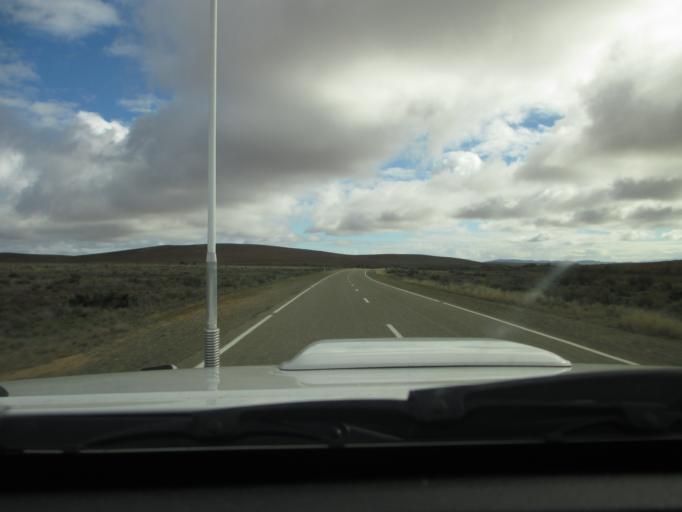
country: AU
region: South Australia
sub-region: Flinders Ranges
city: Quorn
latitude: -32.1405
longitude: 138.5169
